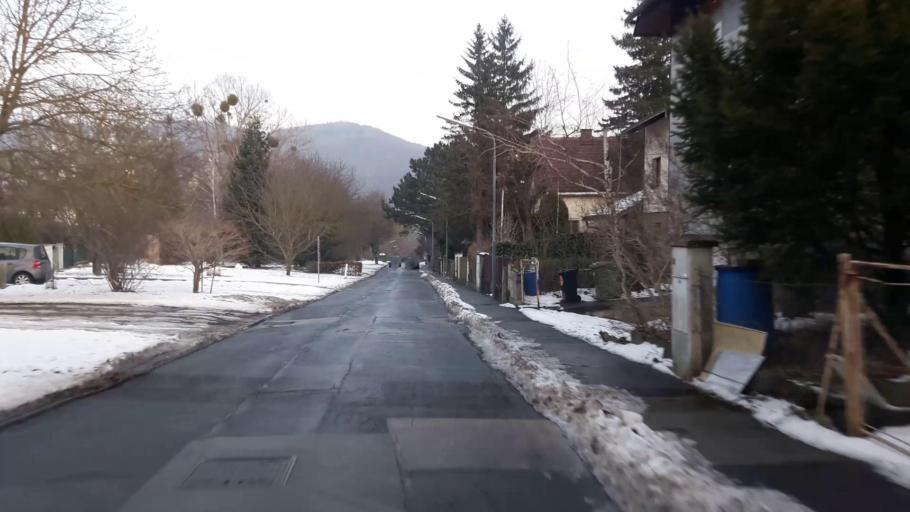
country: AT
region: Lower Austria
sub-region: Politischer Bezirk Wien-Umgebung
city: Purkersdorf
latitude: 48.2140
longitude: 16.2436
